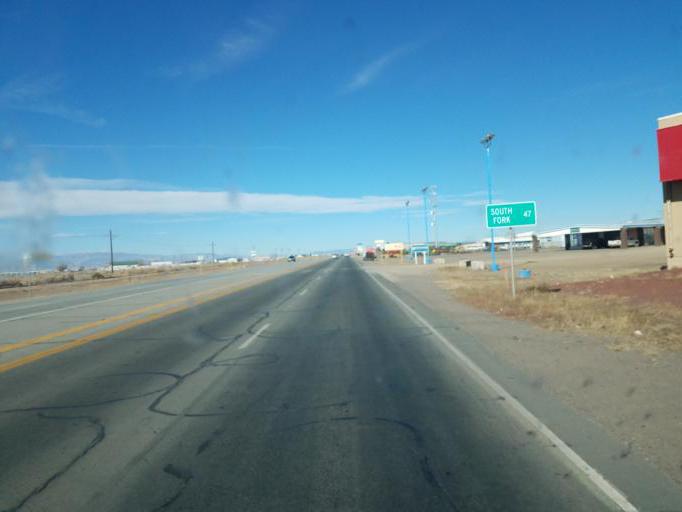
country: US
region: Colorado
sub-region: Alamosa County
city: Alamosa
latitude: 37.4760
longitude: -105.8962
